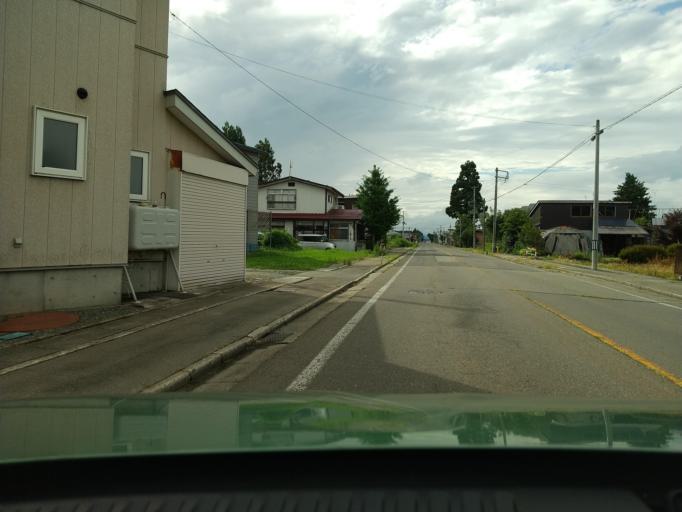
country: JP
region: Akita
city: Yuzawa
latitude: 39.2307
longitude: 140.5159
